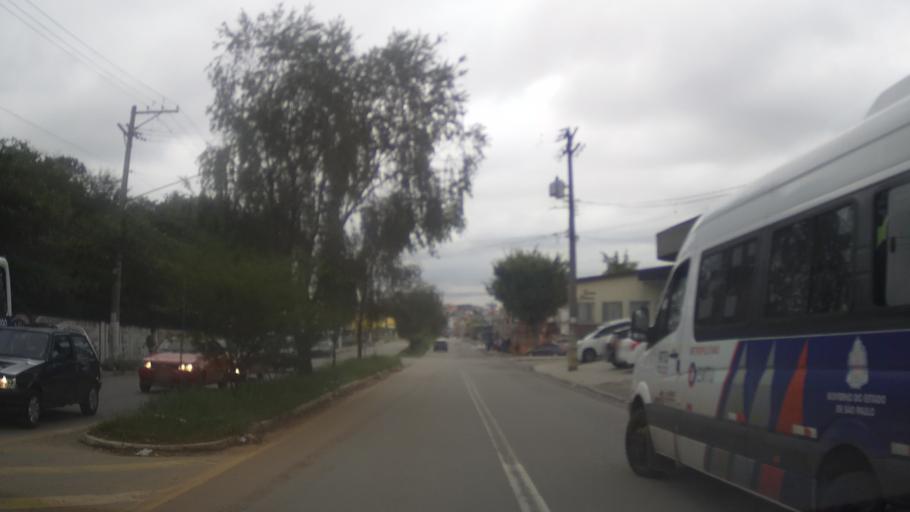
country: BR
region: Sao Paulo
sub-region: Guarulhos
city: Guarulhos
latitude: -23.4240
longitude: -46.5241
